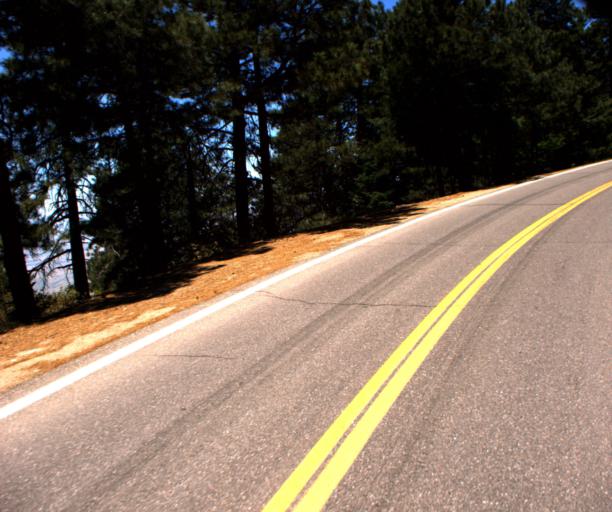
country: US
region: Arizona
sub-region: Graham County
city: Swift Trail Junction
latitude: 32.6286
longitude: -109.8389
